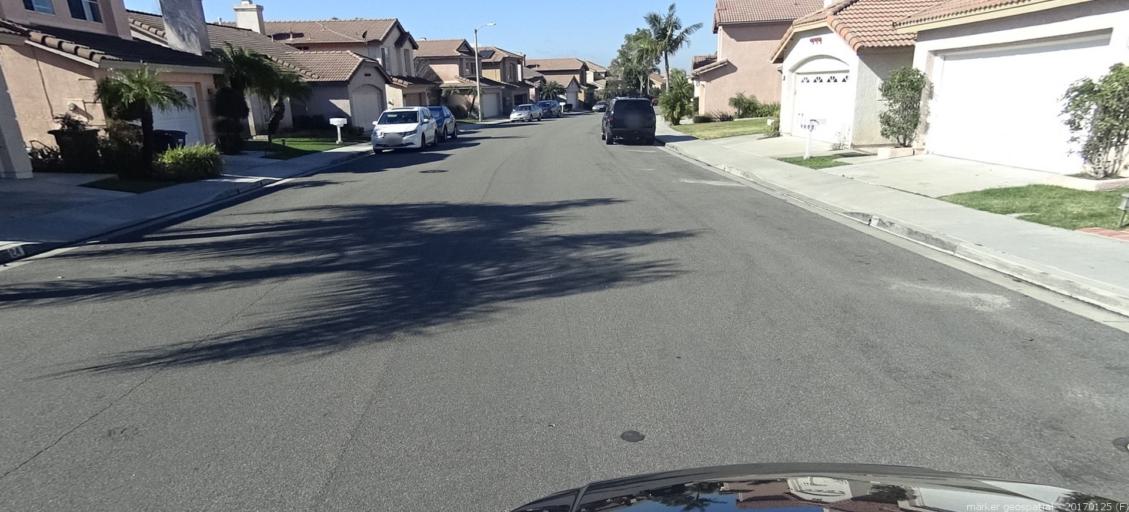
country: US
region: California
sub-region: Orange County
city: Foothill Ranch
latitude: 33.6847
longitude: -117.6526
